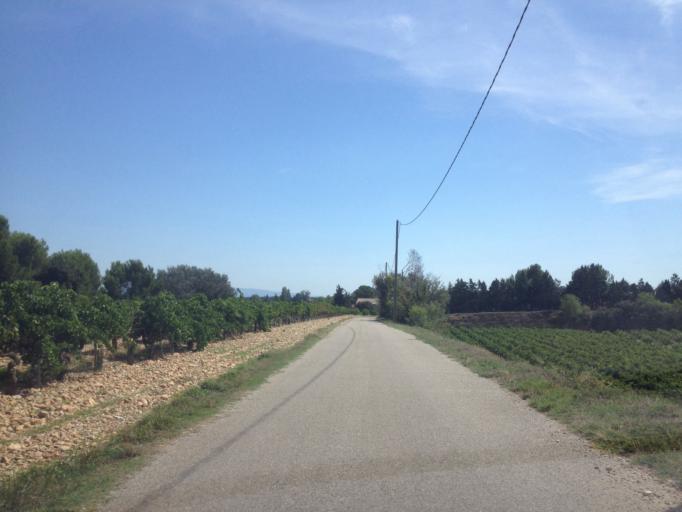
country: FR
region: Provence-Alpes-Cote d'Azur
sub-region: Departement du Vaucluse
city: Bedarrides
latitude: 44.0566
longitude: 4.8921
